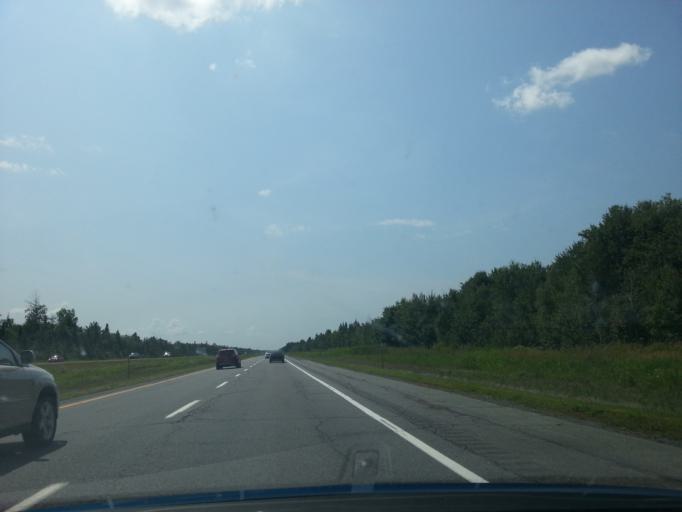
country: CA
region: Quebec
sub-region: Mauricie
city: Princeville
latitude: 46.3007
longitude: -71.9658
